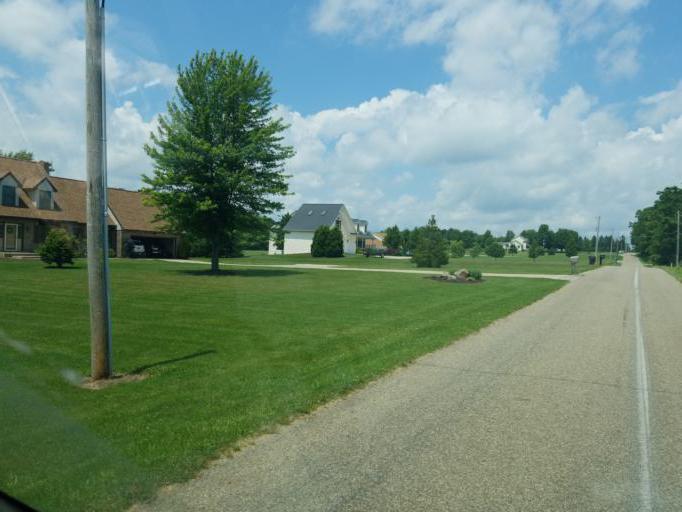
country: US
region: Ohio
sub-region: Richland County
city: Lexington
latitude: 40.6484
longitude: -82.6019
